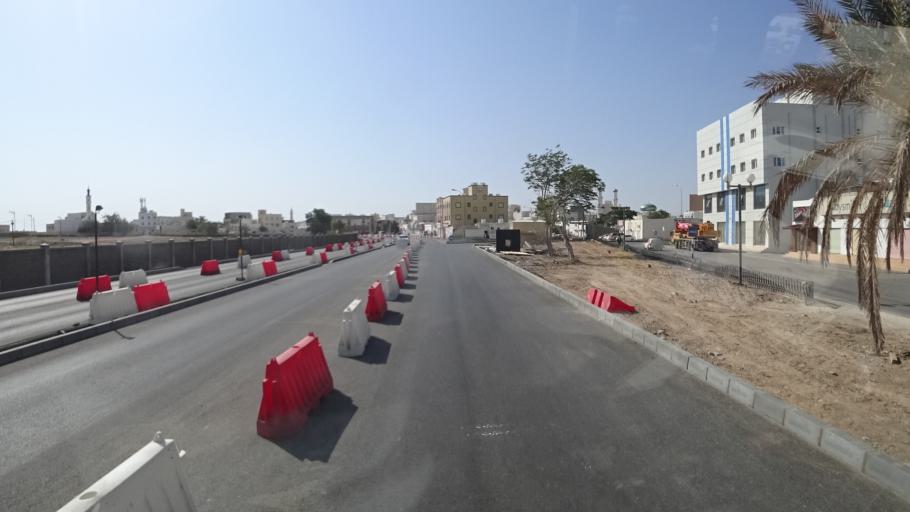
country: OM
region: Ash Sharqiyah
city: Sur
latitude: 22.5733
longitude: 59.5244
